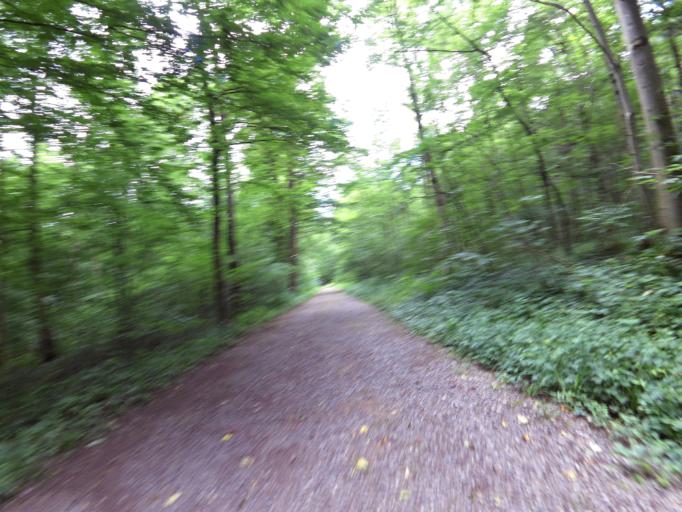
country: CH
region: Zurich
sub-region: Bezirk Zuerich
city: Zuerich (Kreis 10)
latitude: 47.4110
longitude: 8.5006
